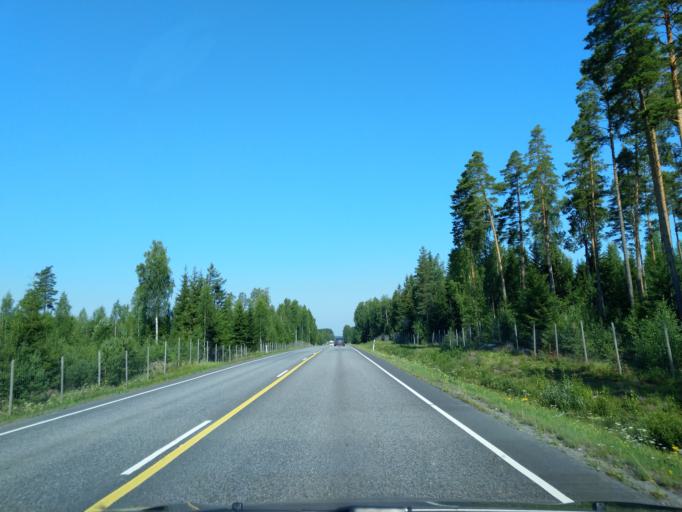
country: FI
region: Pirkanmaa
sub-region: Lounais-Pirkanmaa
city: Punkalaidun
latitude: 61.0224
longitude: 23.0480
